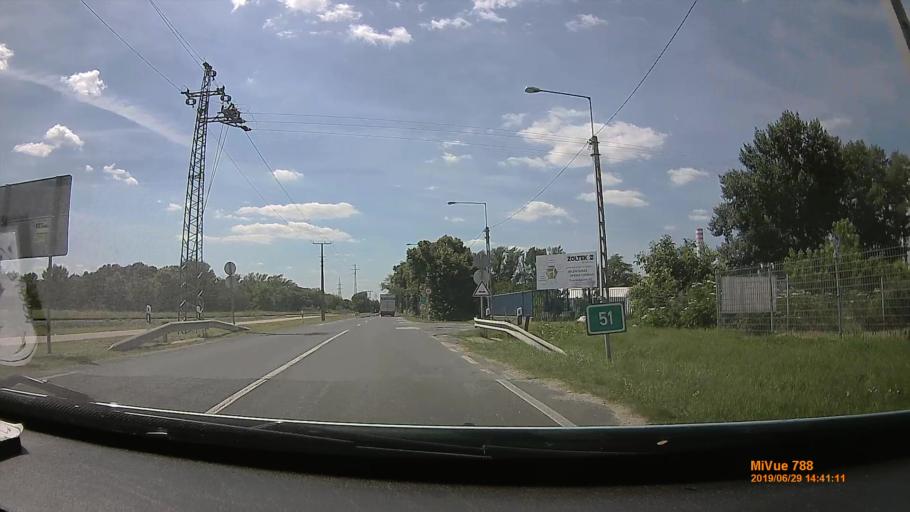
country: HU
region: Komarom-Esztergom
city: Nyergesujfalu
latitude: 47.7574
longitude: 18.5768
